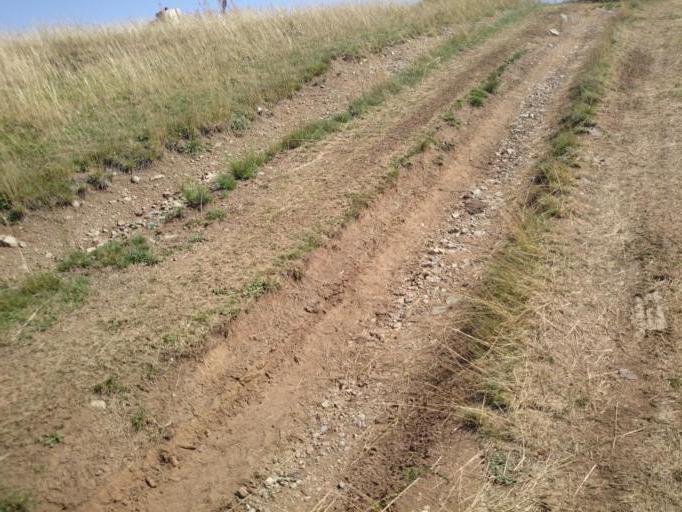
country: AL
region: Elbasan
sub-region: Rrethi i Librazhdit
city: Orenje
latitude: 41.3333
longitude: 20.1735
